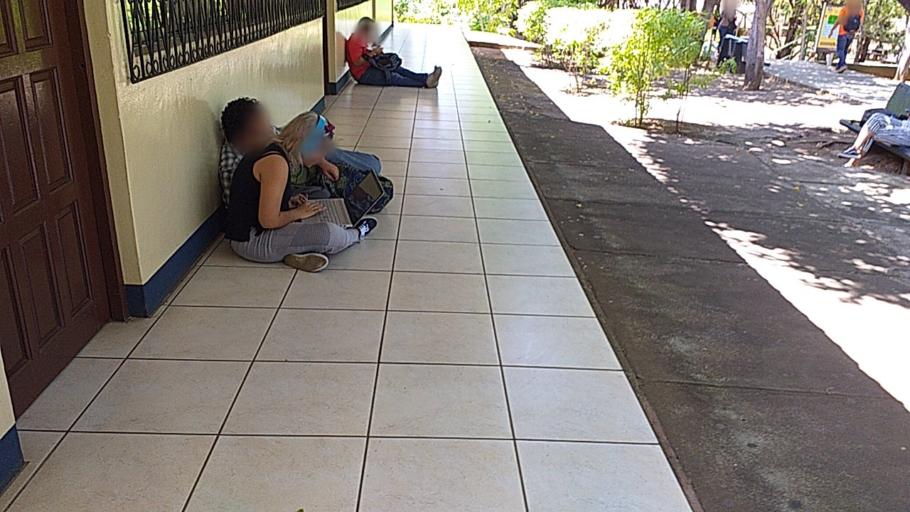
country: NI
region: Managua
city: Managua
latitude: 12.1255
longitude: -86.2706
